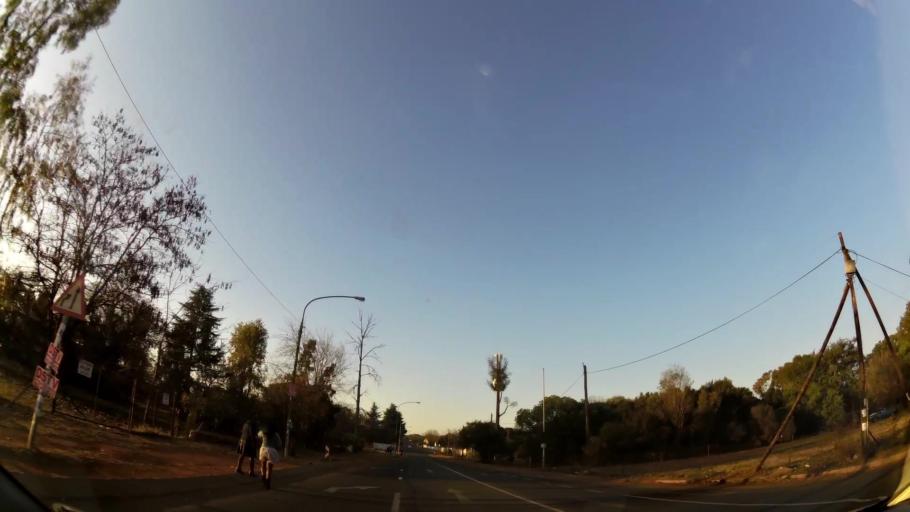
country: ZA
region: Gauteng
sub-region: City of Tshwane Metropolitan Municipality
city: Centurion
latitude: -25.8589
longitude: 28.1981
